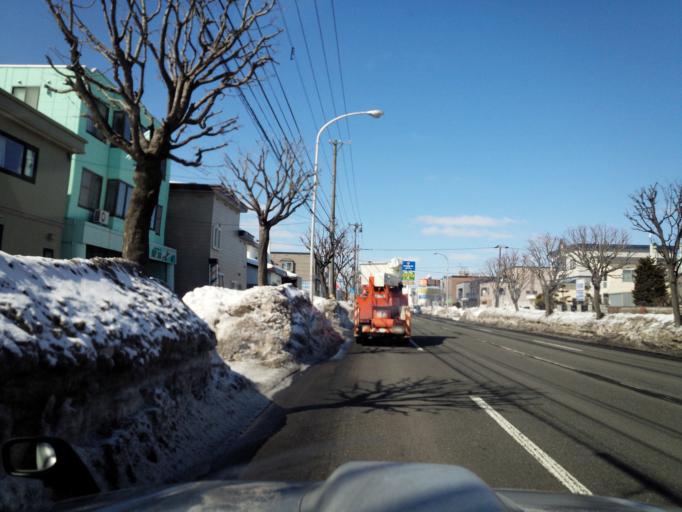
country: JP
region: Hokkaido
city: Sapporo
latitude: 43.0101
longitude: 141.4362
